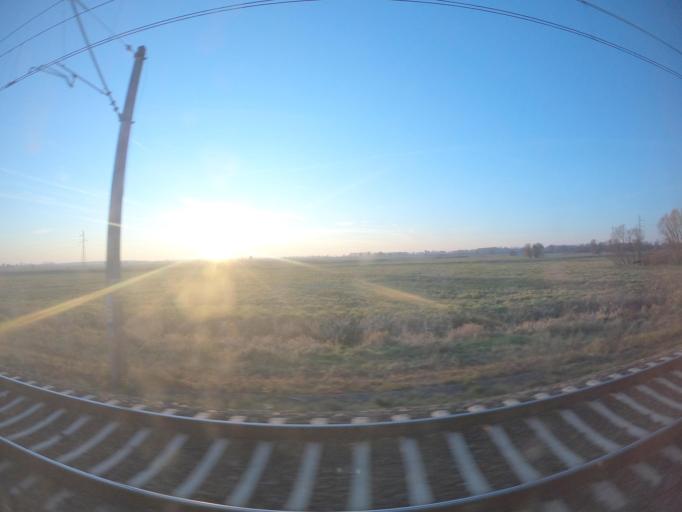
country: PL
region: Lubusz
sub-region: Powiat gorzowski
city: Kostrzyn nad Odra
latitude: 52.5601
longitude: 14.6486
